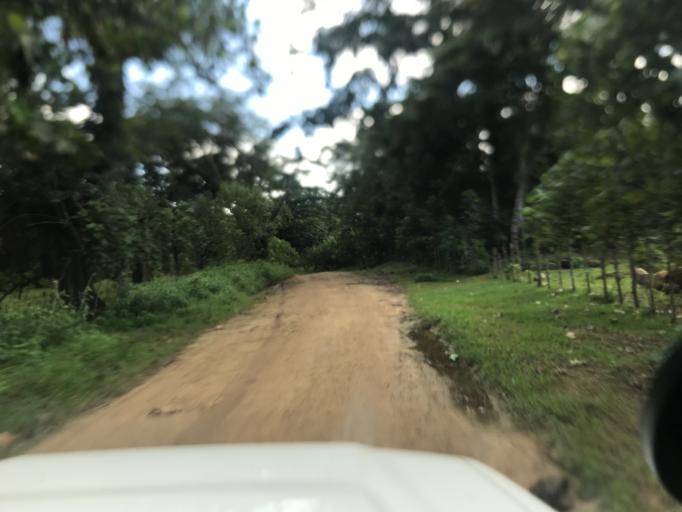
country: VU
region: Sanma
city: Luganville
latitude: -15.4904
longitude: 167.0897
